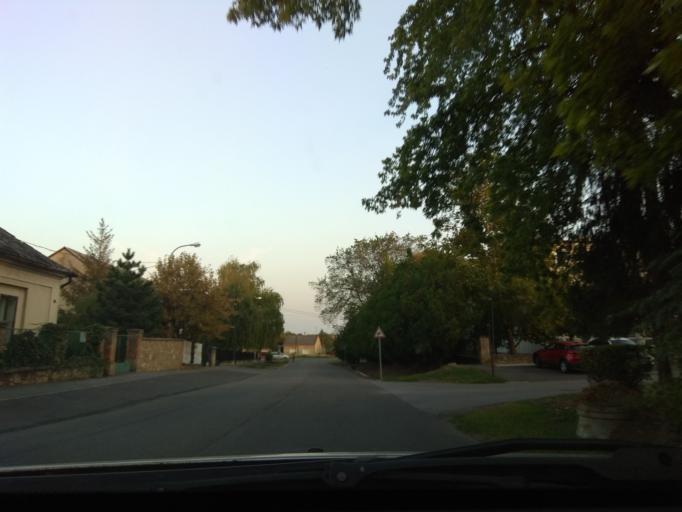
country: HU
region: Borsod-Abauj-Zemplen
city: Szerencs
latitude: 48.1649
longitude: 21.2059
